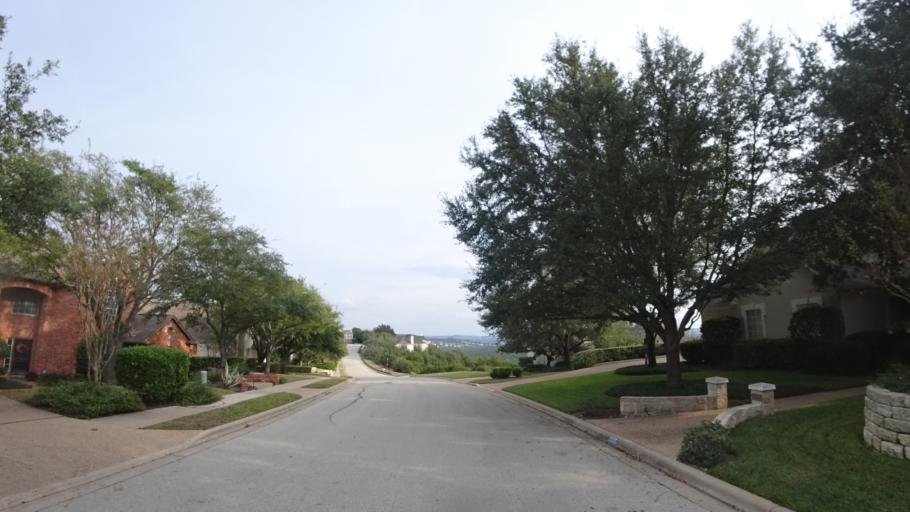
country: US
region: Texas
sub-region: Travis County
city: Hudson Bend
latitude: 30.3755
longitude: -97.8797
